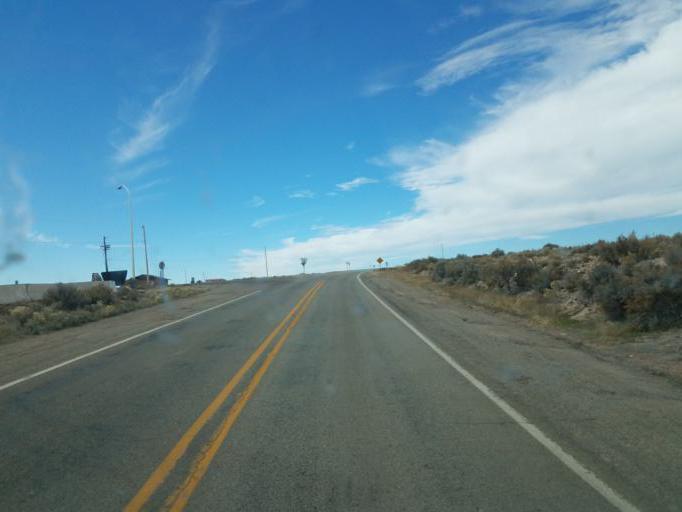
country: US
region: New Mexico
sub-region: Taos County
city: Arroyo Seco
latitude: 36.4762
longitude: -105.7373
